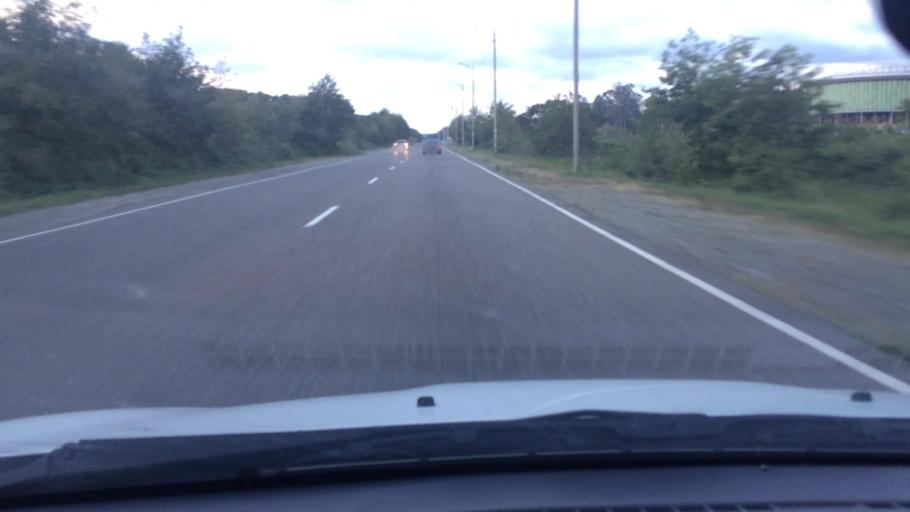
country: GE
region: Guria
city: Urek'i
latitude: 41.9341
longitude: 41.7722
